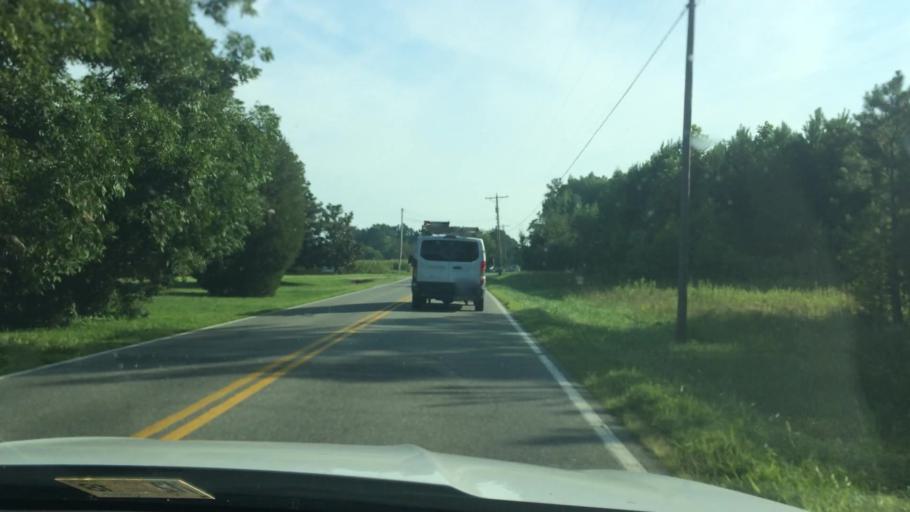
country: US
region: Virginia
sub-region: Gloucester County
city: Gloucester Courthouse
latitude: 37.4820
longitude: -76.4440
